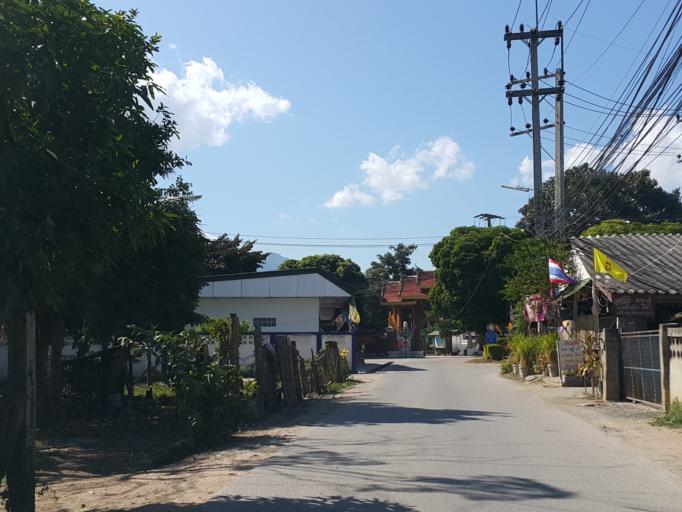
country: TH
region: Chiang Mai
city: Mae Taeng
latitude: 18.9582
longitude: 98.9200
